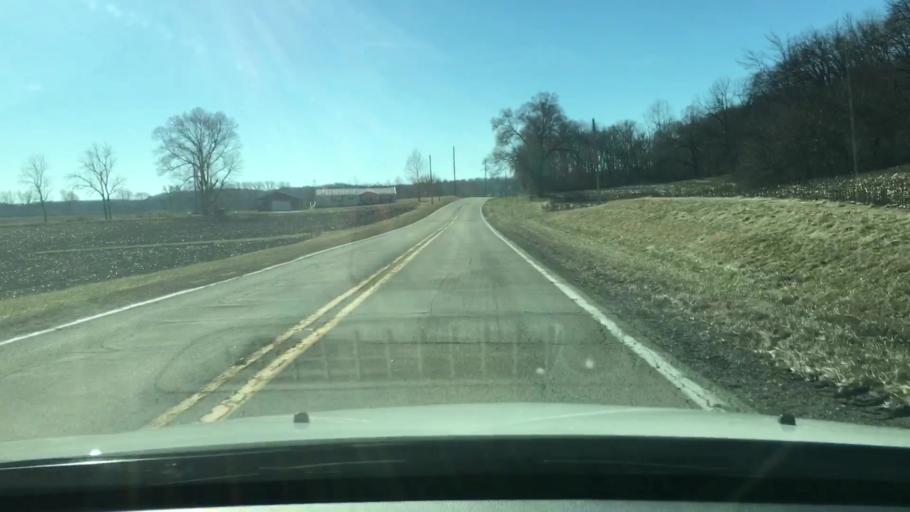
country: US
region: Illinois
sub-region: Mason County
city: Havana
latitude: 40.2338
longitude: -90.1967
